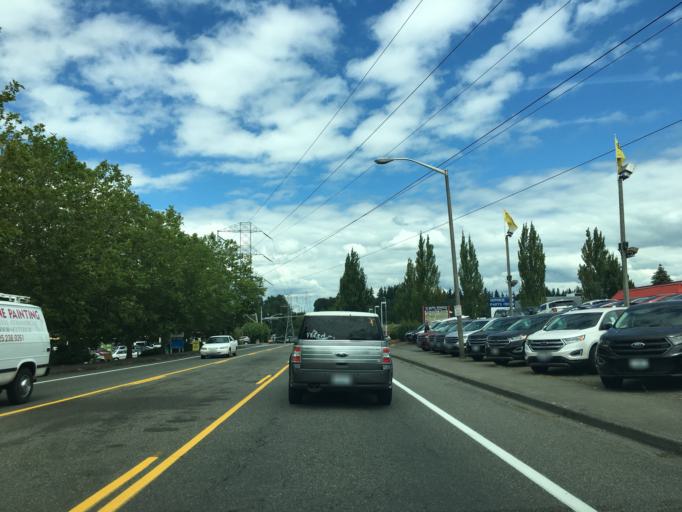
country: US
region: Washington
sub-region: King County
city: Kingsgate
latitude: 47.7063
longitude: -122.1757
